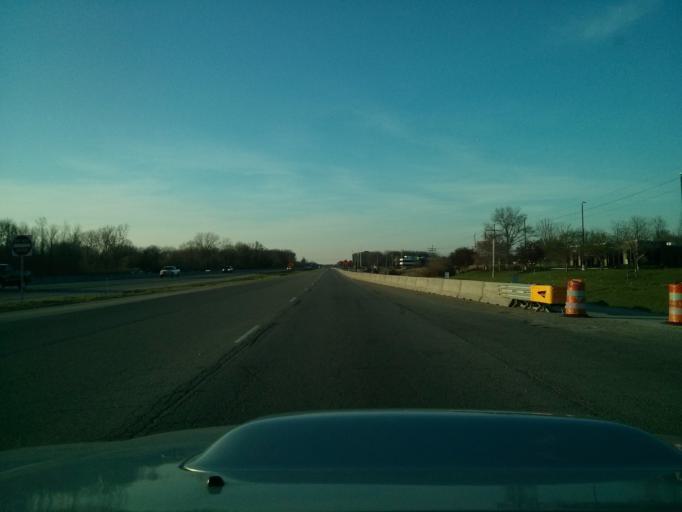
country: US
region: Indiana
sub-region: Marion County
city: Meridian Hills
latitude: 39.9418
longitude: -86.1576
